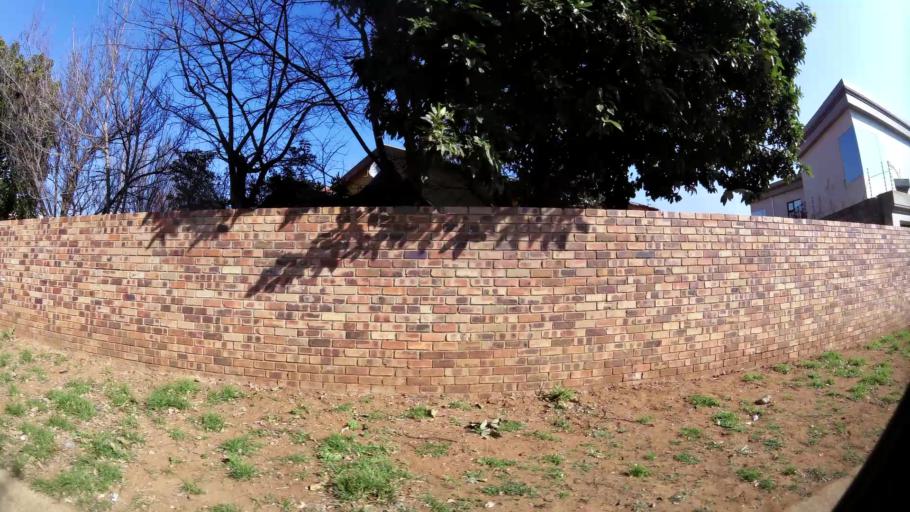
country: ZA
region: Gauteng
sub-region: City of Johannesburg Metropolitan Municipality
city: Johannesburg
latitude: -26.2493
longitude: 27.9617
